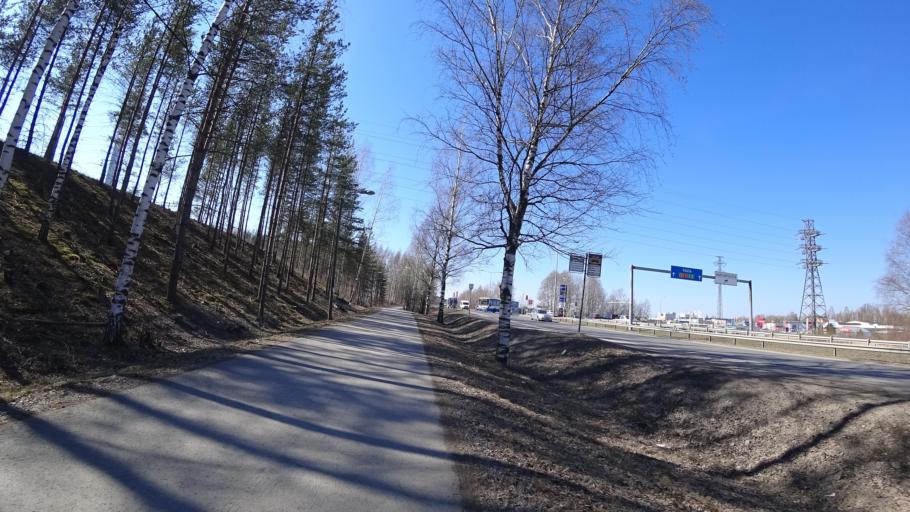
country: FI
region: Pirkanmaa
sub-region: Tampere
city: Pirkkala
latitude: 61.5115
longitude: 23.6786
